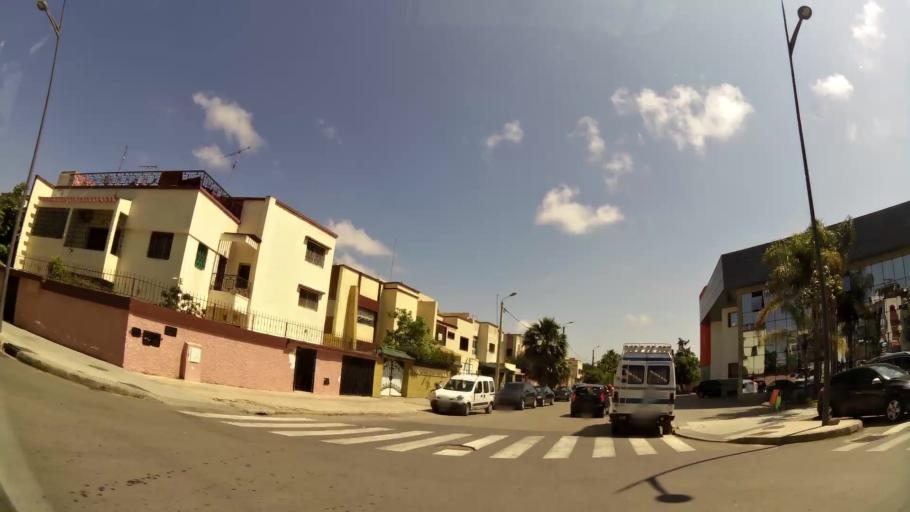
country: MA
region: Rabat-Sale-Zemmour-Zaer
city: Sale
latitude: 34.0465
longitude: -6.7865
